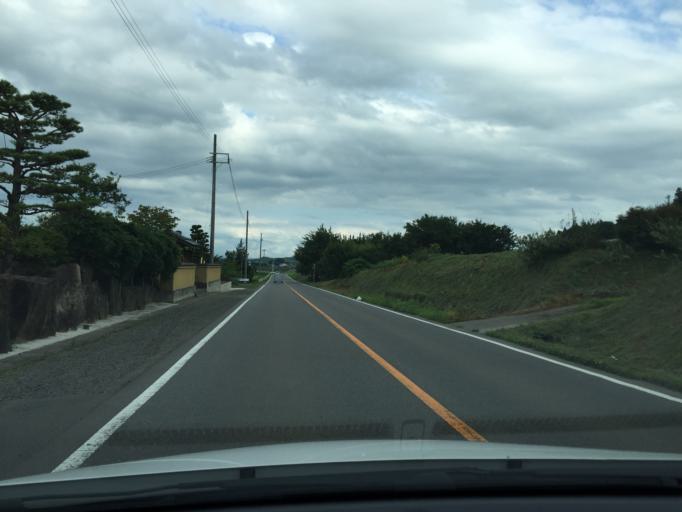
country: JP
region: Fukushima
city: Sukagawa
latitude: 37.2044
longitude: 140.2677
